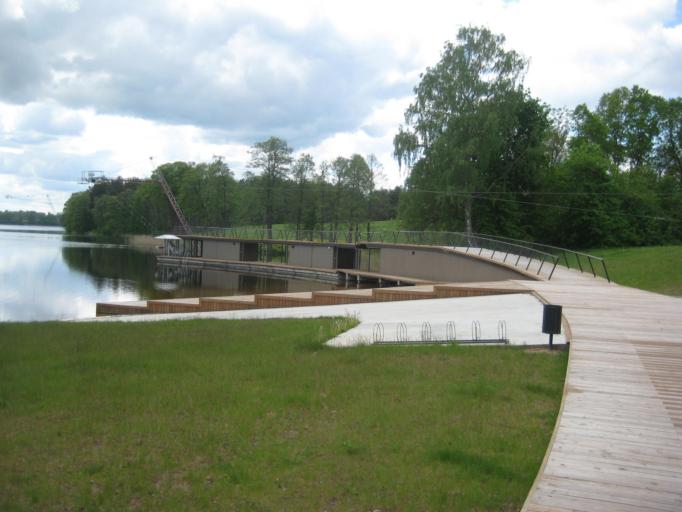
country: LT
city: Zarasai
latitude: 55.7355
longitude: 26.2309
